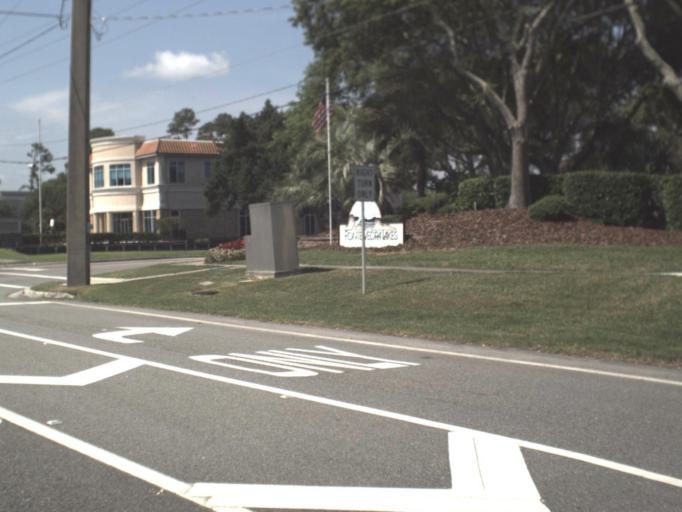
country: US
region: Florida
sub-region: Saint Johns County
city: Ponte Vedra Beach
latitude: 30.2488
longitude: -81.3879
